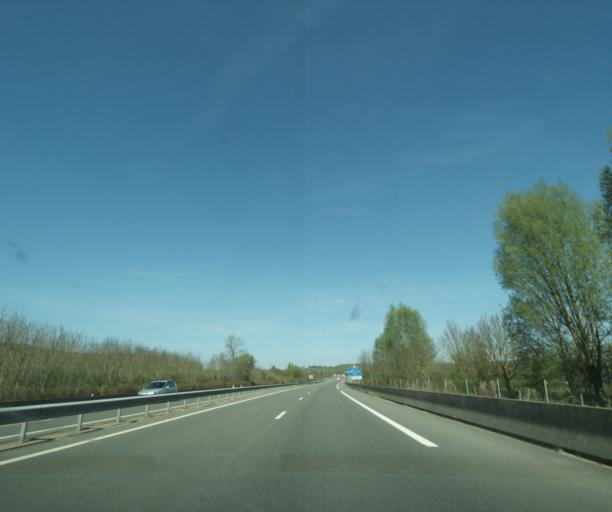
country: FR
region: Bourgogne
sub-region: Departement de la Nievre
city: Pougues-les-Eaux
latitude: 47.0661
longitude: 3.1290
